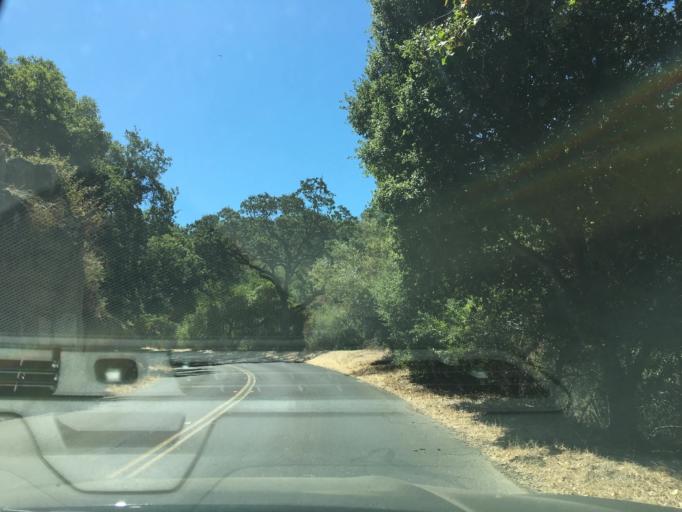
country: US
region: California
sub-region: Santa Clara County
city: East Foothills
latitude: 37.3943
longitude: -121.8189
